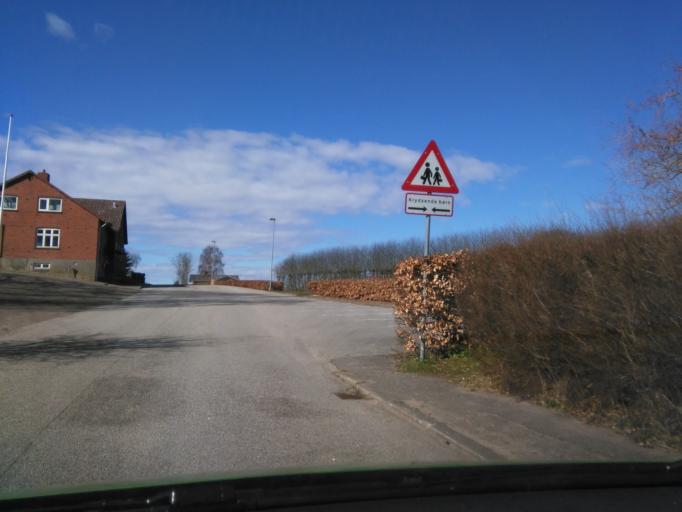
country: DK
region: Central Jutland
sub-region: Skanderborg Kommune
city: Skanderborg
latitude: 55.9625
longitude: 9.9790
